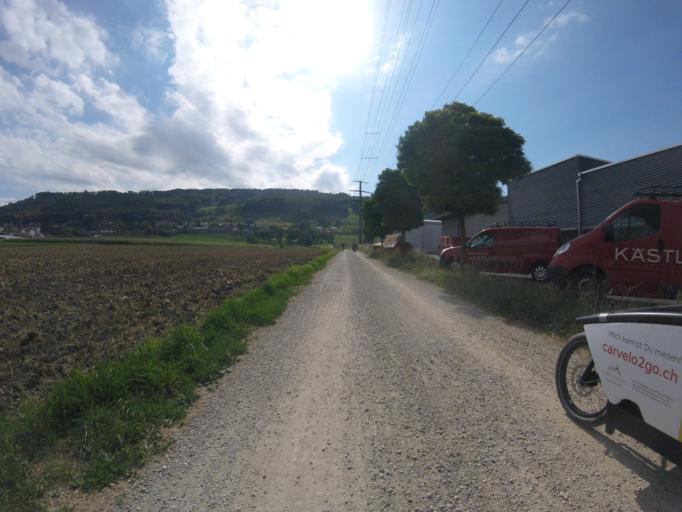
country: CH
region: Bern
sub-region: Bern-Mittelland District
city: Belp
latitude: 46.9035
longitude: 7.4957
